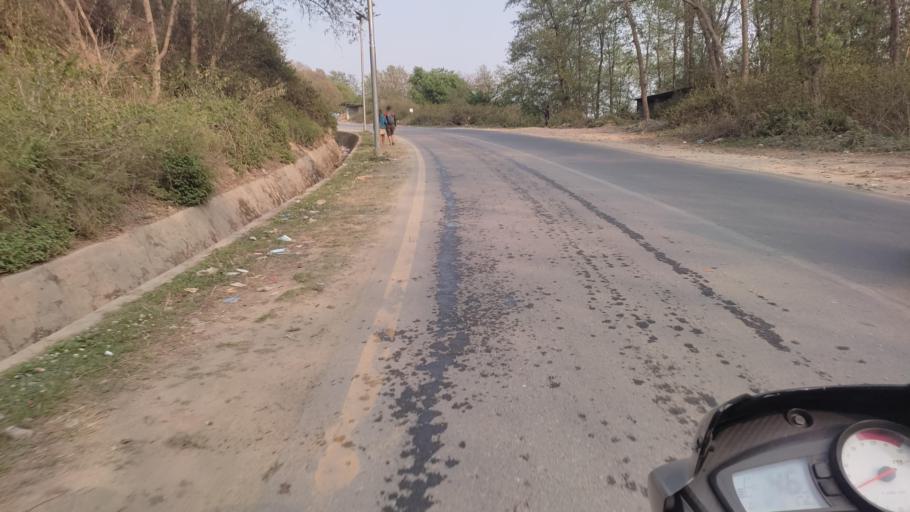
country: NP
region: Central Region
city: Kirtipur
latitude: 27.6609
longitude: 85.2908
